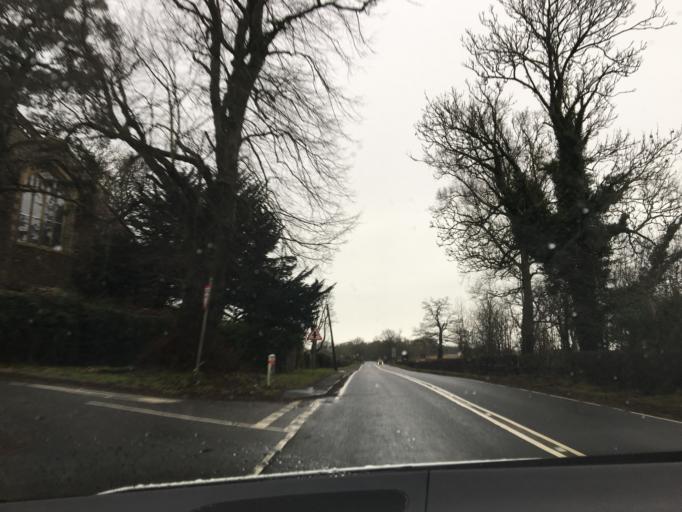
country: GB
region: Scotland
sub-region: Stirling
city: Doune
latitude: 56.1649
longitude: -4.0633
